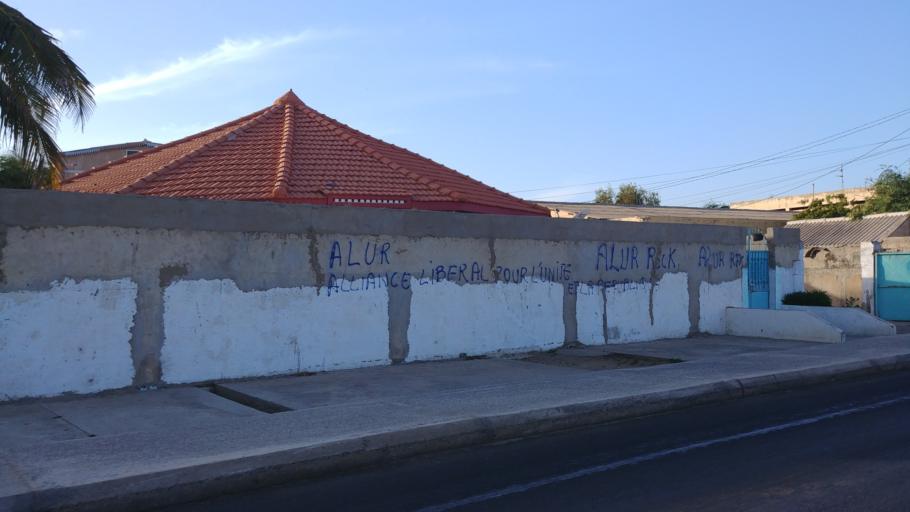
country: SN
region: Saint-Louis
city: Saint-Louis
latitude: 16.0181
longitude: -16.4995
